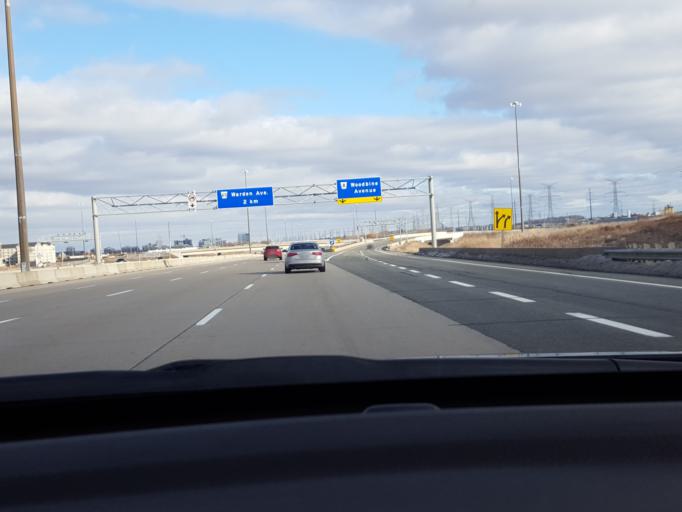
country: CA
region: Ontario
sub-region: York
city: Richmond Hill
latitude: 43.8395
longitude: -79.3637
